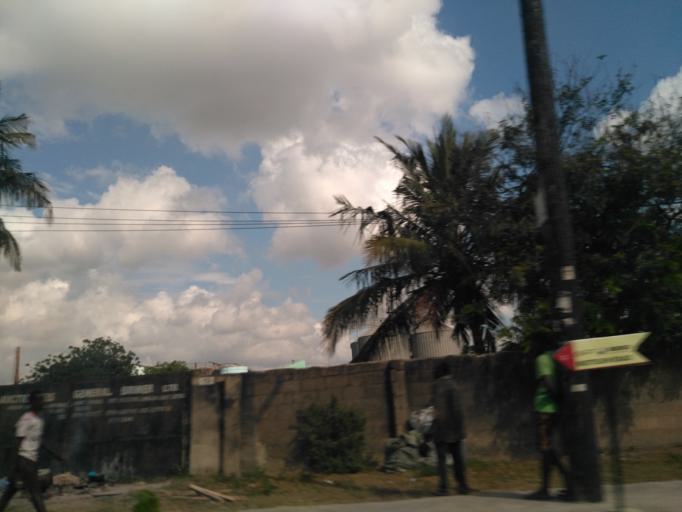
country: TZ
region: Dar es Salaam
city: Magomeni
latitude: -6.7610
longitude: 39.2383
